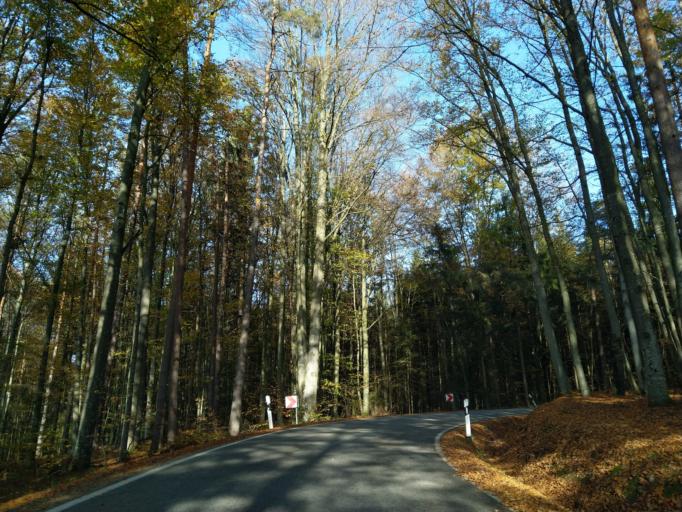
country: DE
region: Bavaria
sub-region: Lower Bavaria
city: Grattersdorf
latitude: 48.7944
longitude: 13.1772
